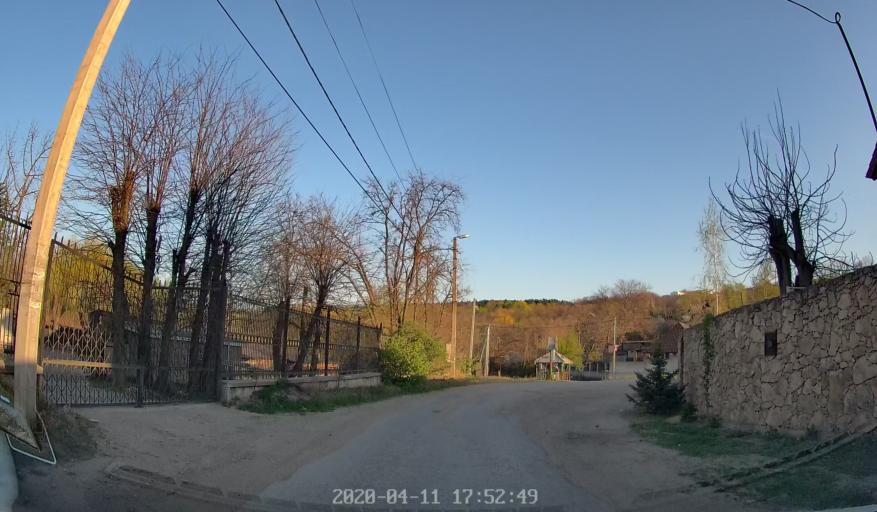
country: MD
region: Chisinau
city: Chisinau
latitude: 46.9719
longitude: 28.8647
